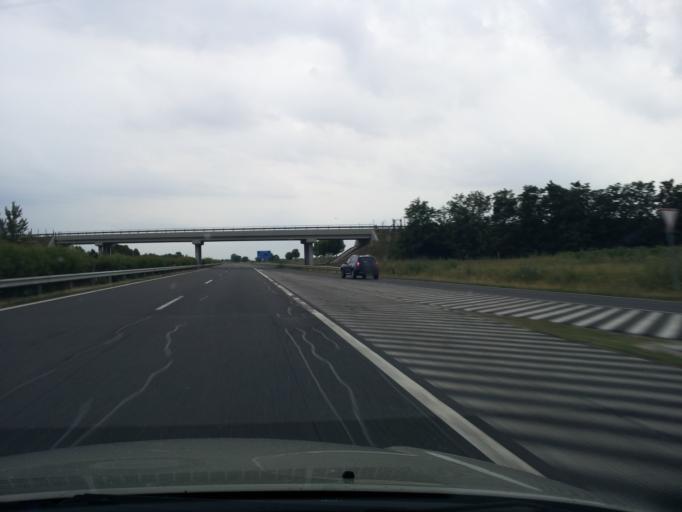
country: HU
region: Borsod-Abauj-Zemplen
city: Emod
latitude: 47.9188
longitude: 20.8451
